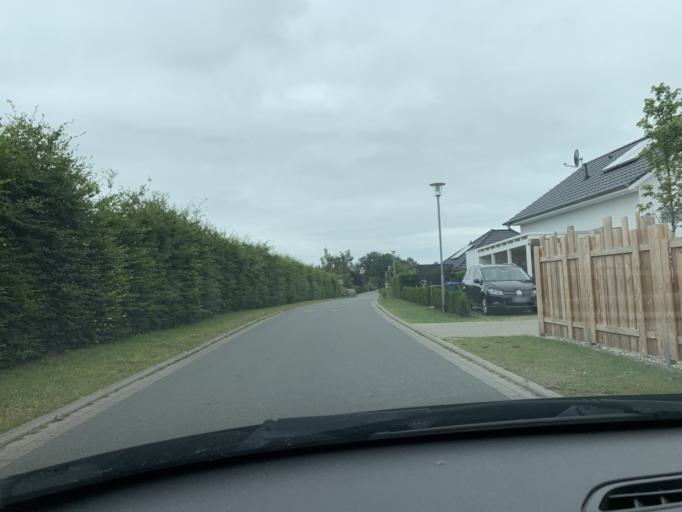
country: DE
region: Lower Saxony
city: Westerstede
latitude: 53.2460
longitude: 7.9070
